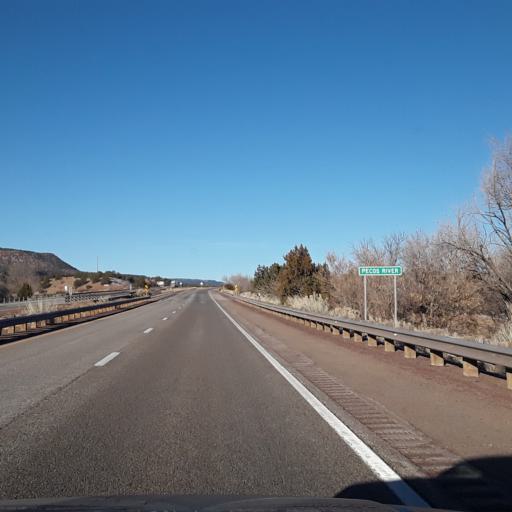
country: US
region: New Mexico
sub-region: San Miguel County
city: Pecos
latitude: 35.4000
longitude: -105.4739
